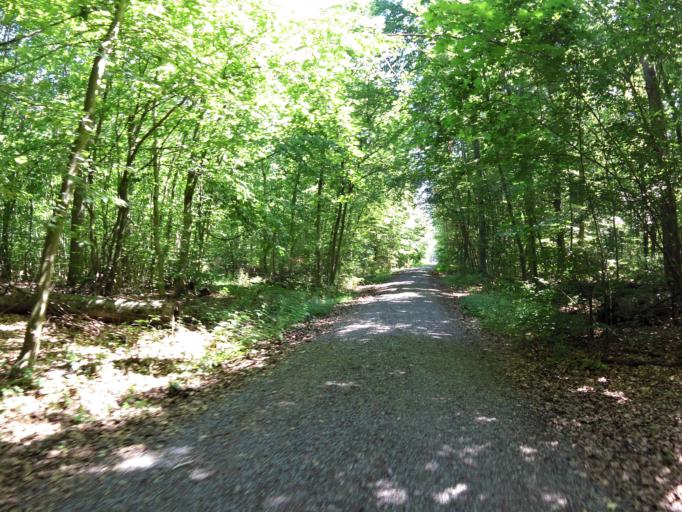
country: DE
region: Bavaria
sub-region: Regierungsbezirk Unterfranken
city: Kleinrinderfeld
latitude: 49.7046
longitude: 9.8611
